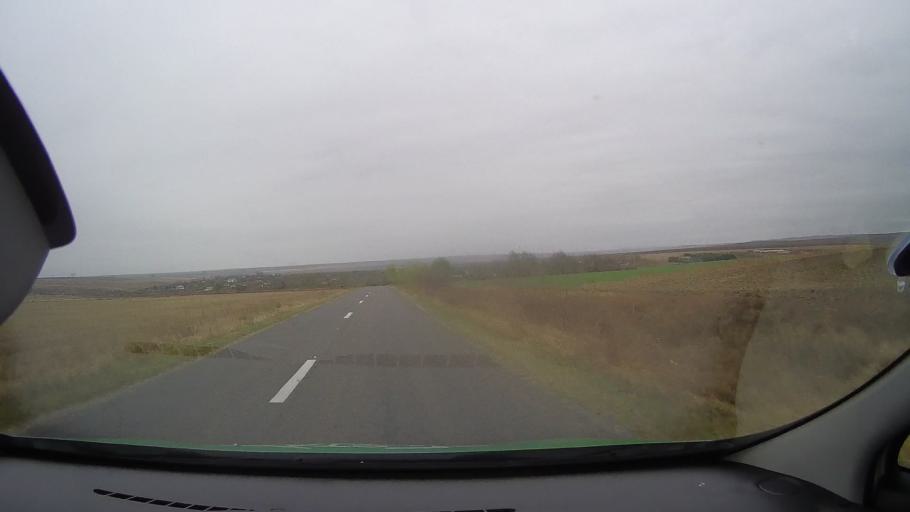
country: RO
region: Constanta
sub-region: Comuna Vulturu
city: Vulturu
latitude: 44.6949
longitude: 28.2420
